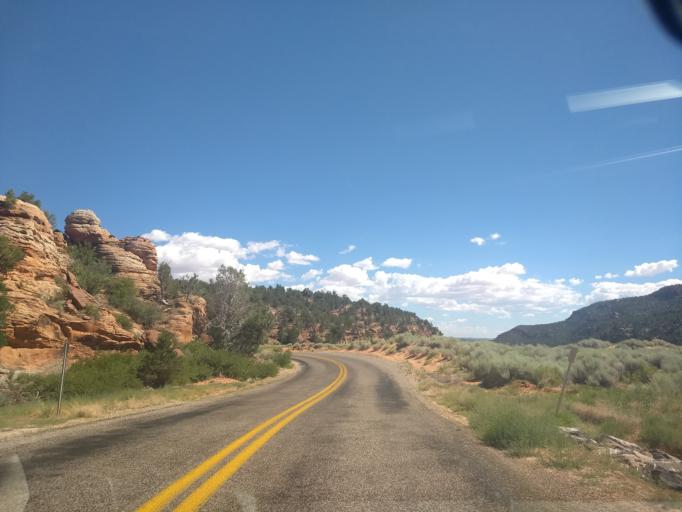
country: US
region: Utah
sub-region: Washington County
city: Hildale
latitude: 36.9879
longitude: -112.8686
